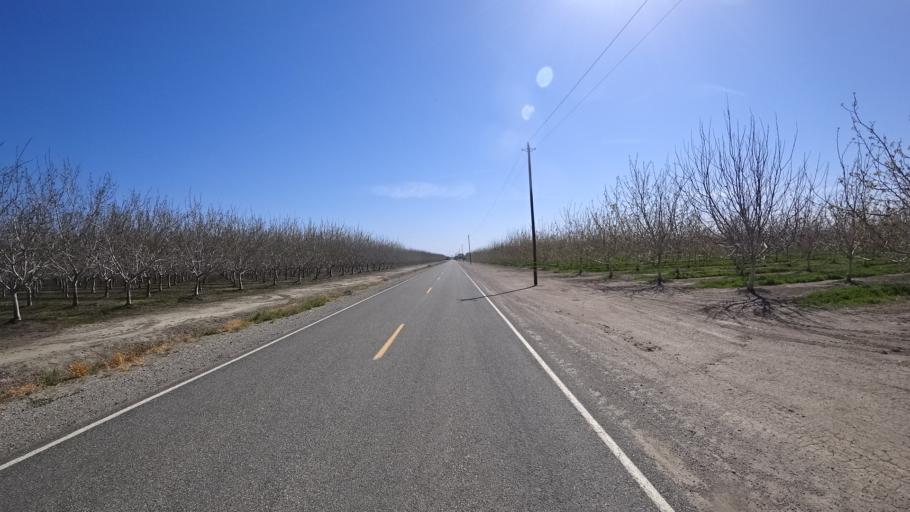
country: US
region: California
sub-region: Glenn County
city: Willows
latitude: 39.6235
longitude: -122.1127
